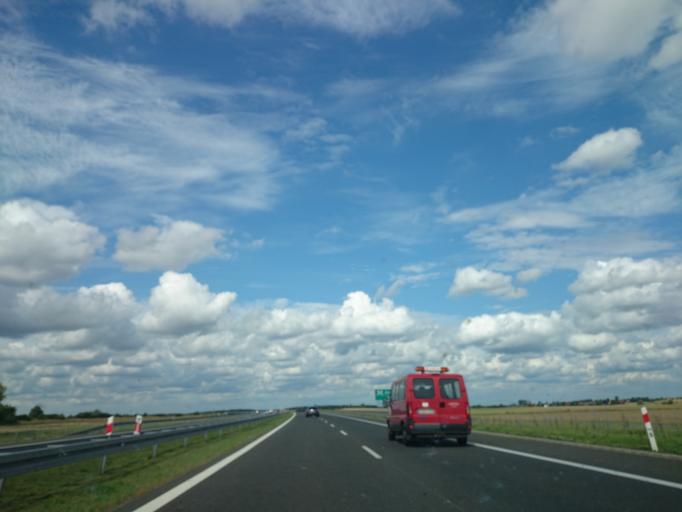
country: PL
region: Lubusz
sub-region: Powiat swiebodzinski
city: Swiebodzin
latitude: 52.2896
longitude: 15.5424
